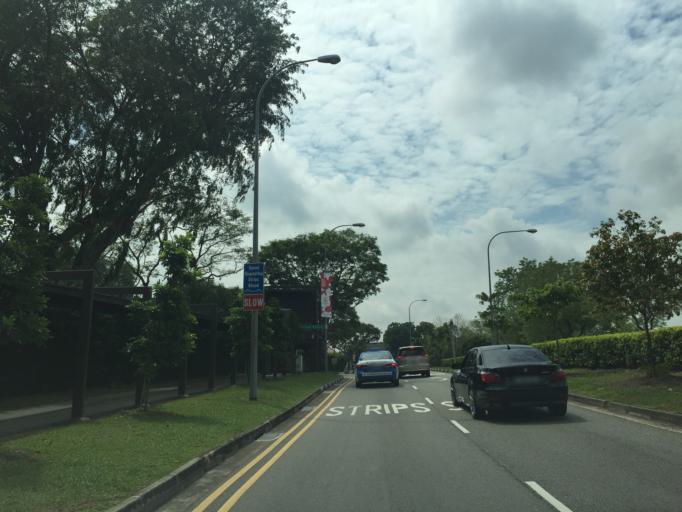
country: SG
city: Singapore
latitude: 1.3234
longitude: 103.8154
